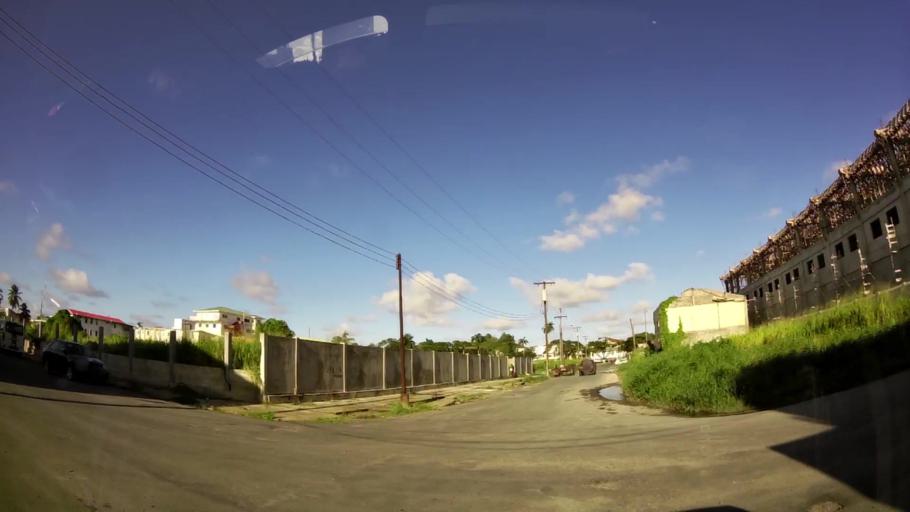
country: GY
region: Demerara-Mahaica
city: Georgetown
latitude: 6.8174
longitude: -58.1660
